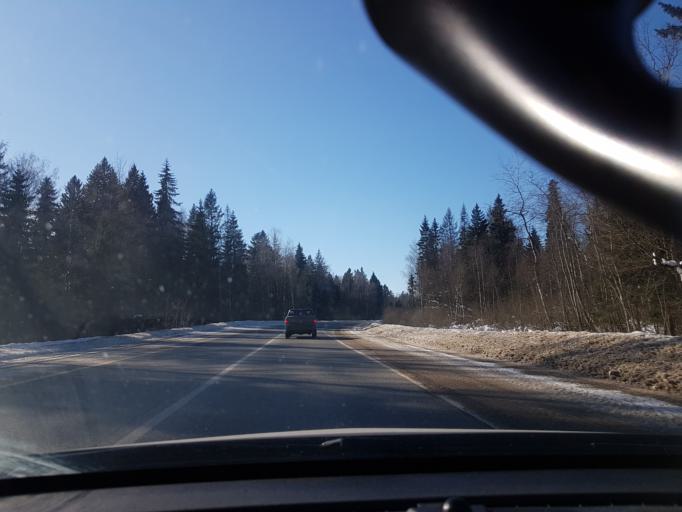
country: RU
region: Moskovskaya
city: Kostrovo
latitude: 55.9130
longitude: 36.7107
